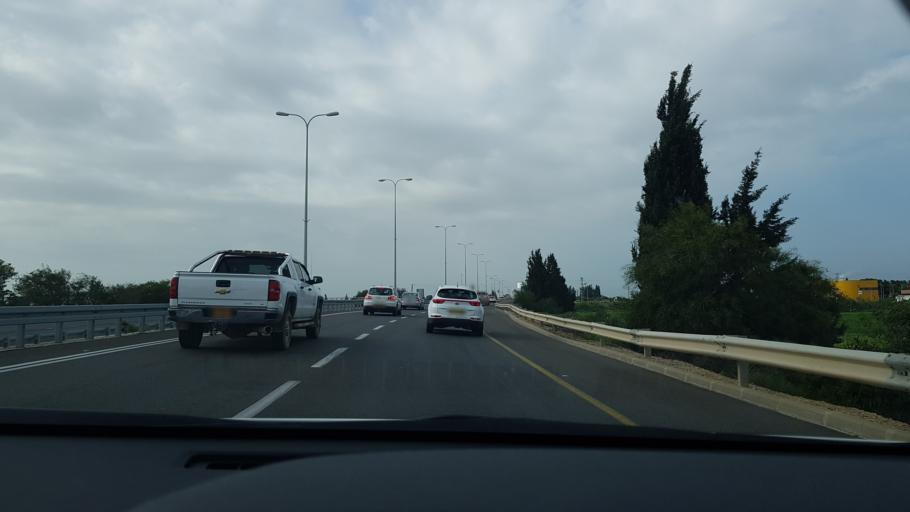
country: IL
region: Southern District
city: Ashqelon
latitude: 31.6615
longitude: 34.6057
